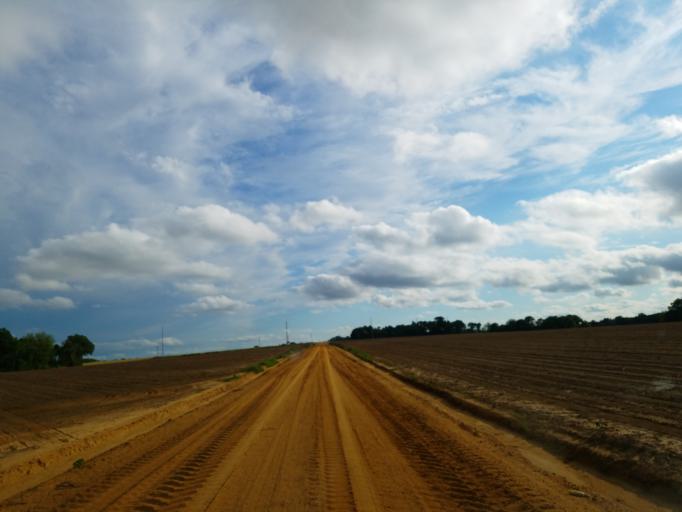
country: US
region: Georgia
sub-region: Dooly County
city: Vienna
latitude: 32.1490
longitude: -83.7786
